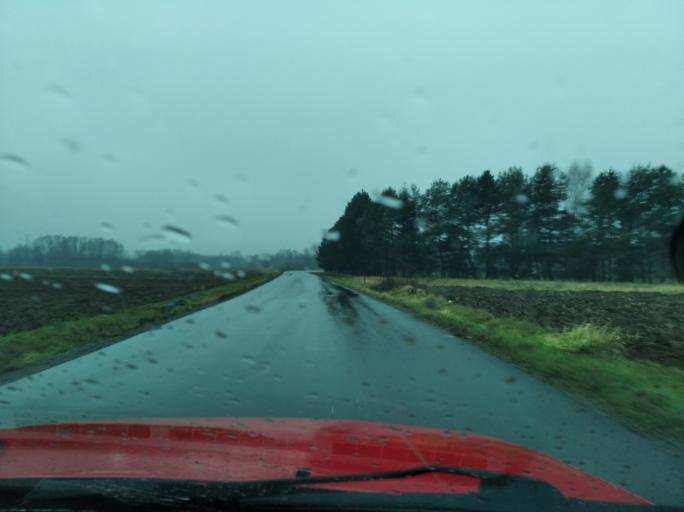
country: PL
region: Subcarpathian Voivodeship
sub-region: Powiat lancucki
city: Krzemienica
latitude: 50.0844
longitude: 22.1644
